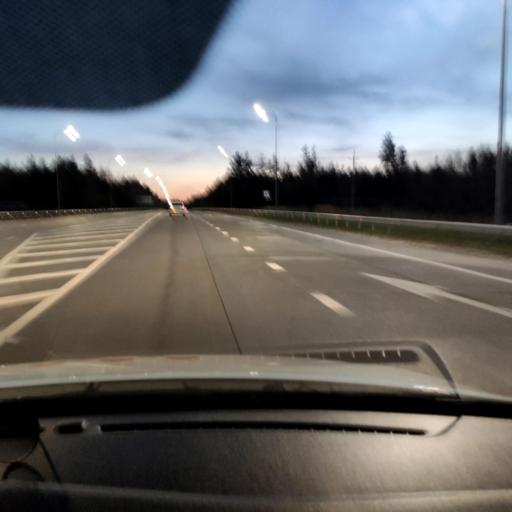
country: RU
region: Tatarstan
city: Stolbishchi
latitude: 55.6397
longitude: 49.1143
